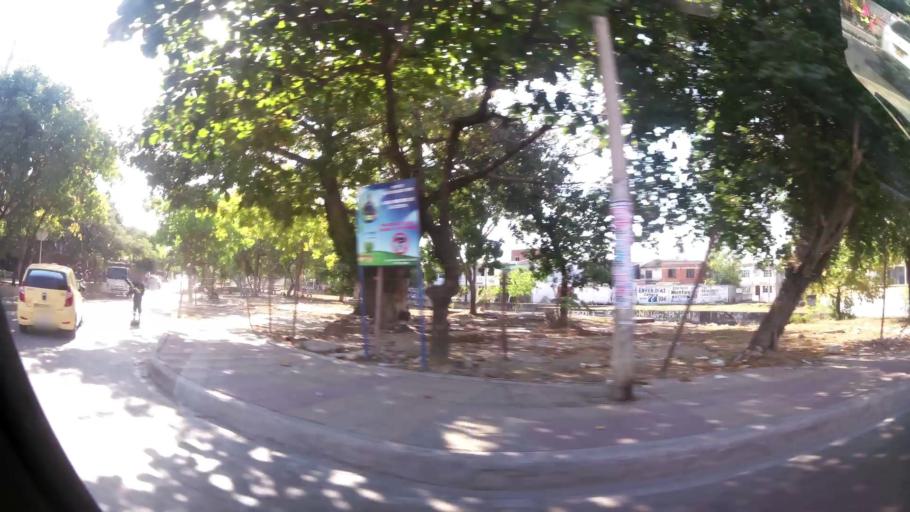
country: CO
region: Bolivar
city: Cartagena
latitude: 10.3928
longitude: -75.4842
